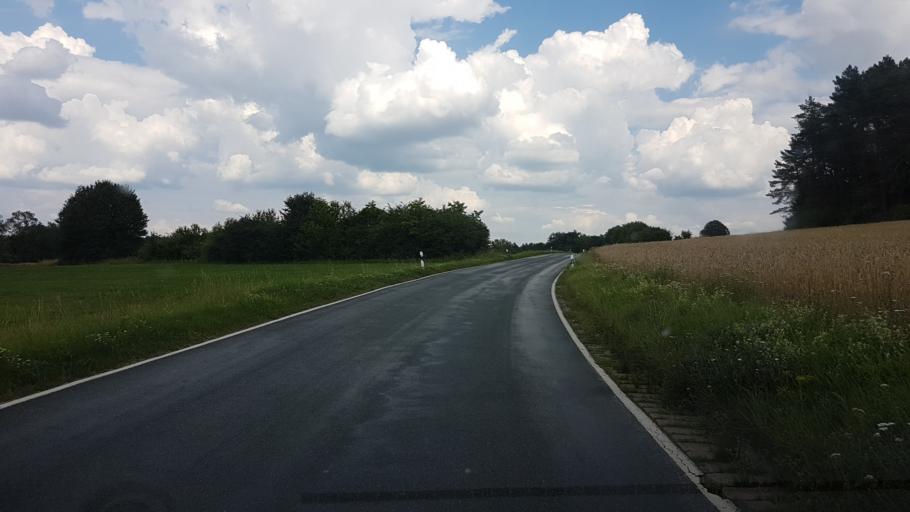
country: DE
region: Bavaria
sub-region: Upper Franconia
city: Gossweinstein
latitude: 49.7654
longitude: 11.2938
